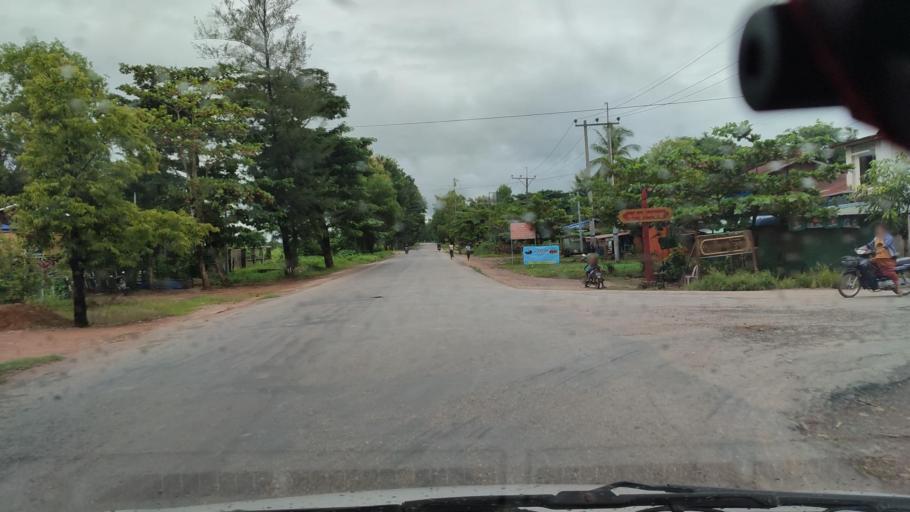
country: MM
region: Bago
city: Letpandan
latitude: 17.8890
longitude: 95.7511
